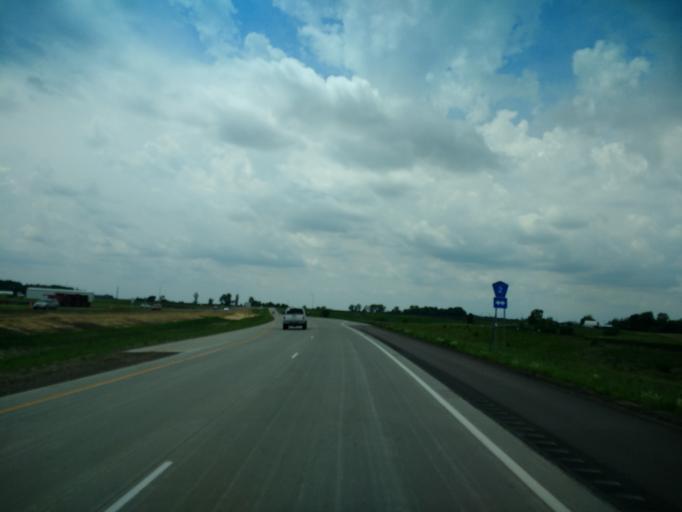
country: US
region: Minnesota
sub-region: Cottonwood County
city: Windom
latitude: 43.9085
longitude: -95.0549
